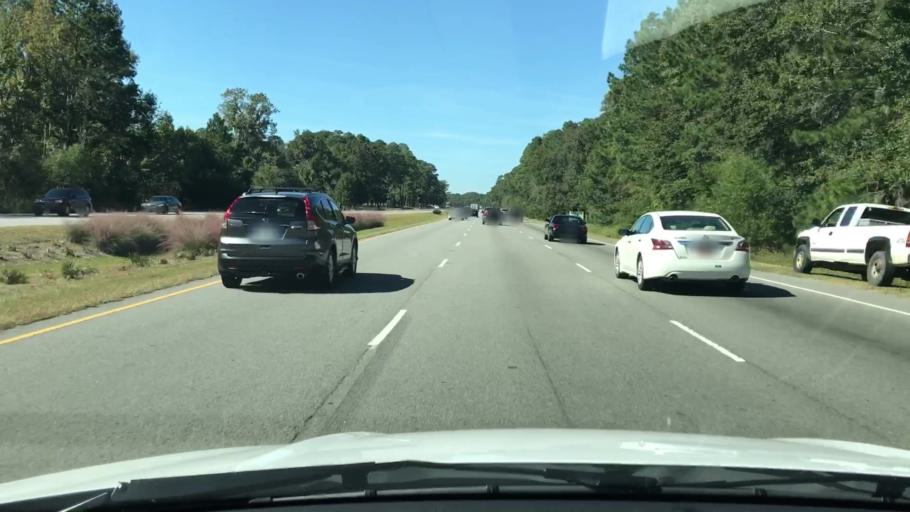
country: US
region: South Carolina
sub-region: Beaufort County
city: Bluffton
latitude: 32.2815
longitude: -80.8764
